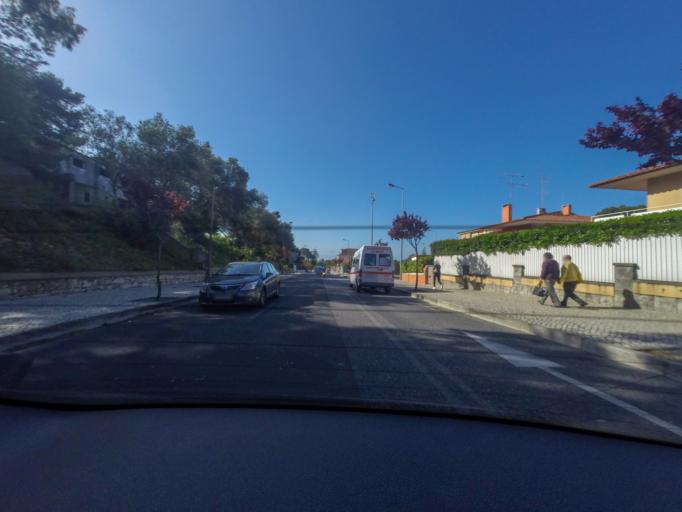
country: PT
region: Lisbon
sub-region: Cascais
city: Monte Estoril
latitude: 38.7069
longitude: -9.4183
